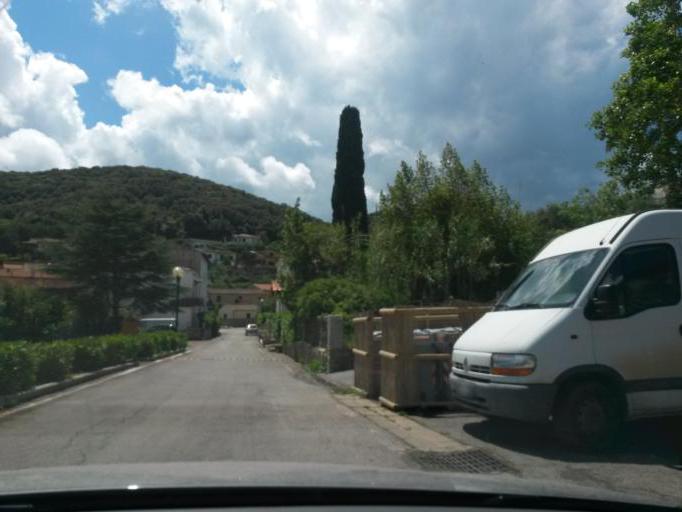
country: IT
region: Tuscany
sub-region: Provincia di Livorno
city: Rio Marina
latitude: 42.8590
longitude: 10.4185
